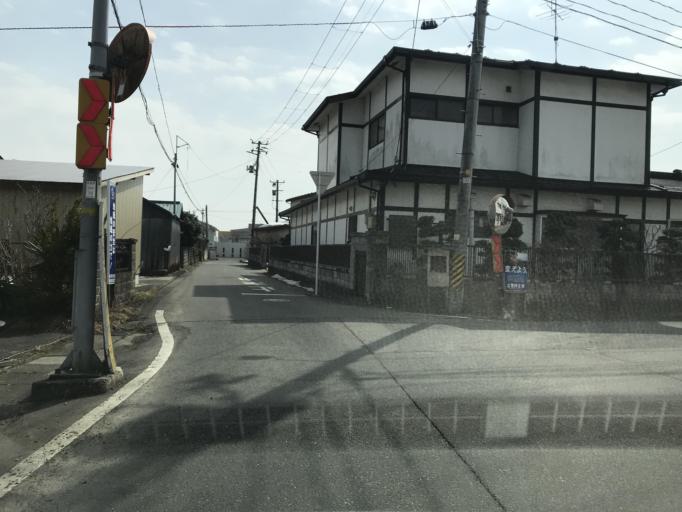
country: JP
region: Miyagi
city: Furukawa
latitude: 38.6592
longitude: 140.8679
